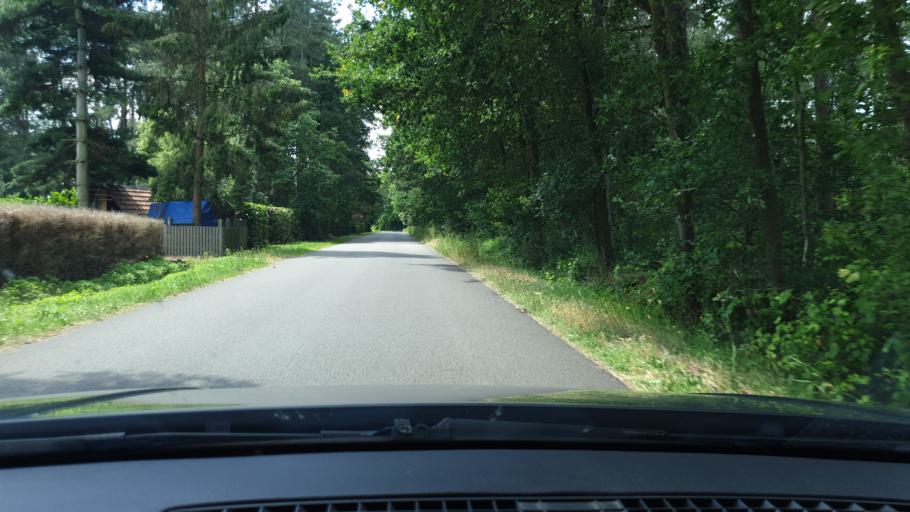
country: BE
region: Flanders
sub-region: Provincie Antwerpen
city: Geel
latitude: 51.1927
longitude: 4.9689
